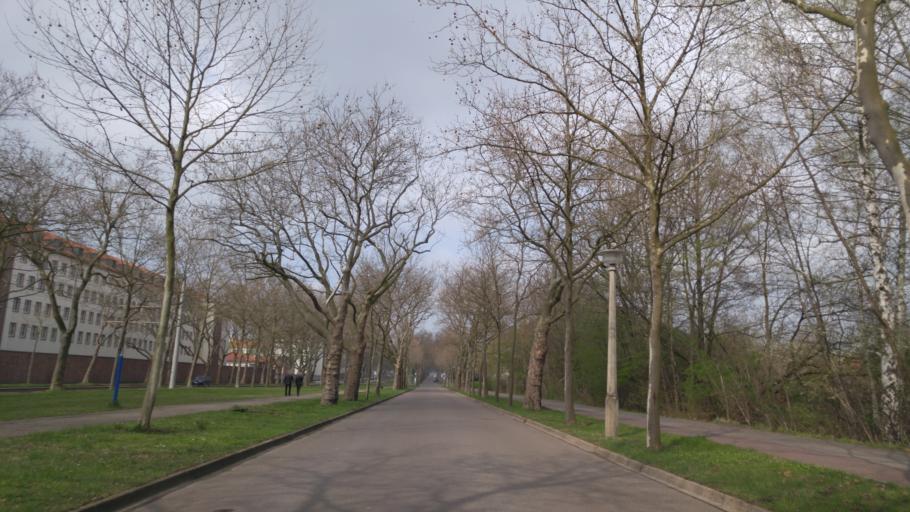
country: DE
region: Saxony-Anhalt
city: Halle Neustadt
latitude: 51.4966
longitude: 11.9384
